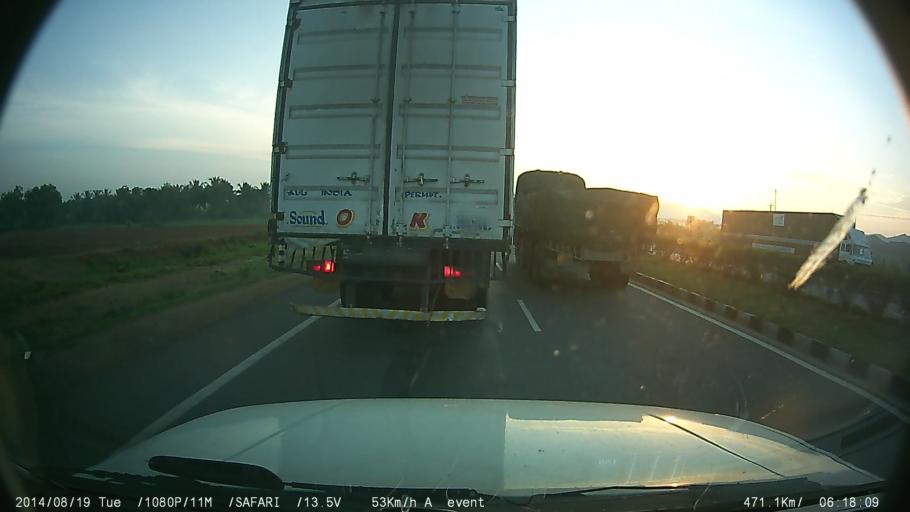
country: IN
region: Tamil Nadu
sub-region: Dharmapuri
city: Dharmapuri
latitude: 12.0007
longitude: 78.0755
